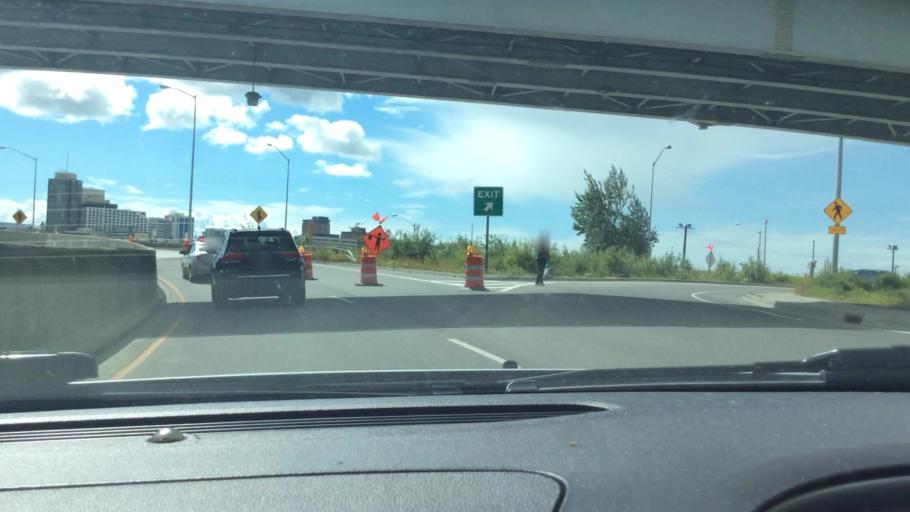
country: US
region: Alaska
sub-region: Anchorage Municipality
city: Anchorage
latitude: 61.2269
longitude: -149.8845
